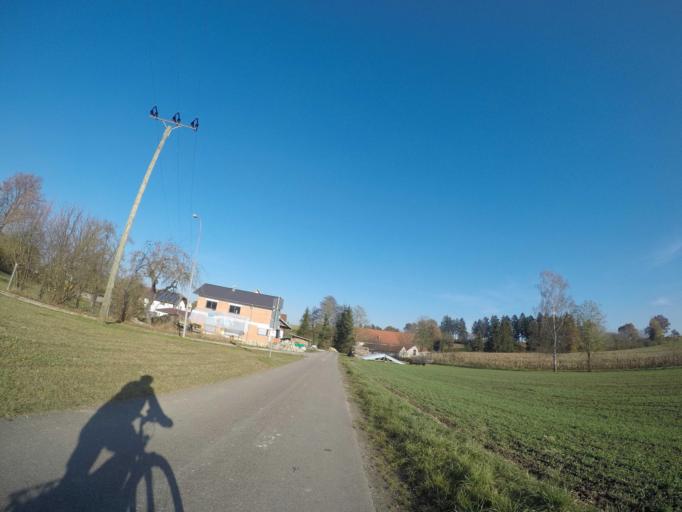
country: DE
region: Baden-Wuerttemberg
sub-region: Tuebingen Region
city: Oberstadion
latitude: 48.1883
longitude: 9.6783
